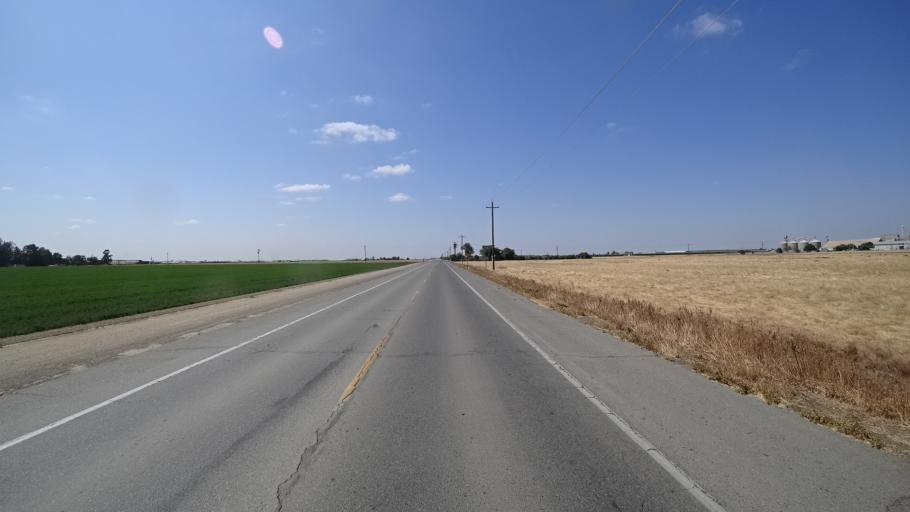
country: US
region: California
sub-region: Kings County
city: Home Garden
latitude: 36.2722
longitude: -119.6370
